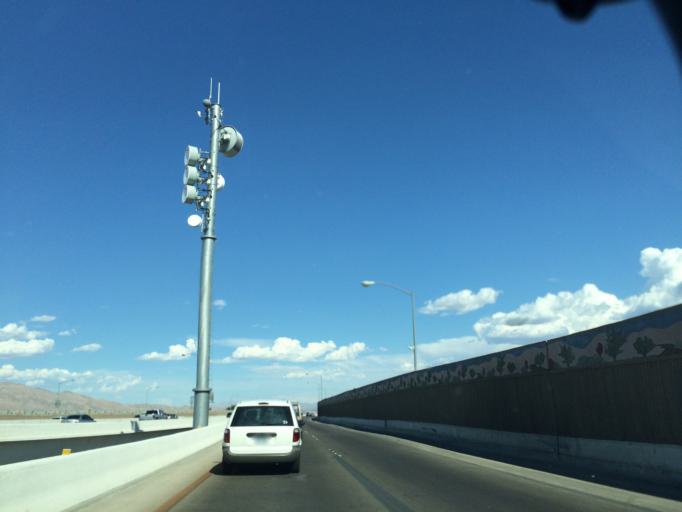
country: US
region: Nevada
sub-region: Clark County
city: Las Vegas
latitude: 36.1725
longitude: -115.1357
